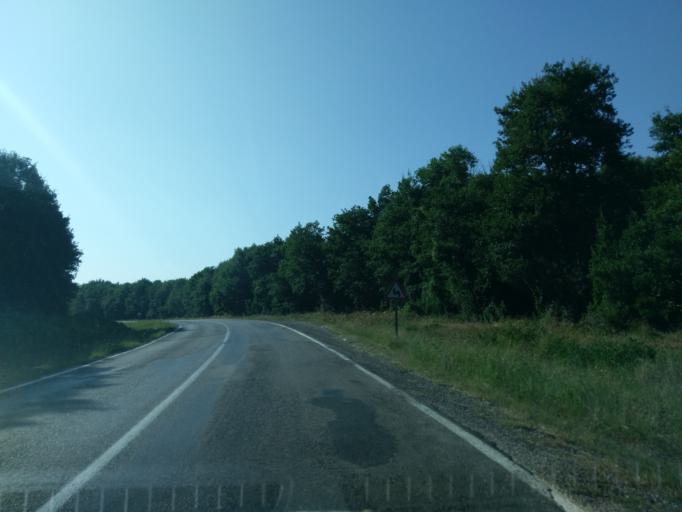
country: TR
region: Sinop
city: Yenikonak
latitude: 41.9444
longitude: 34.7390
